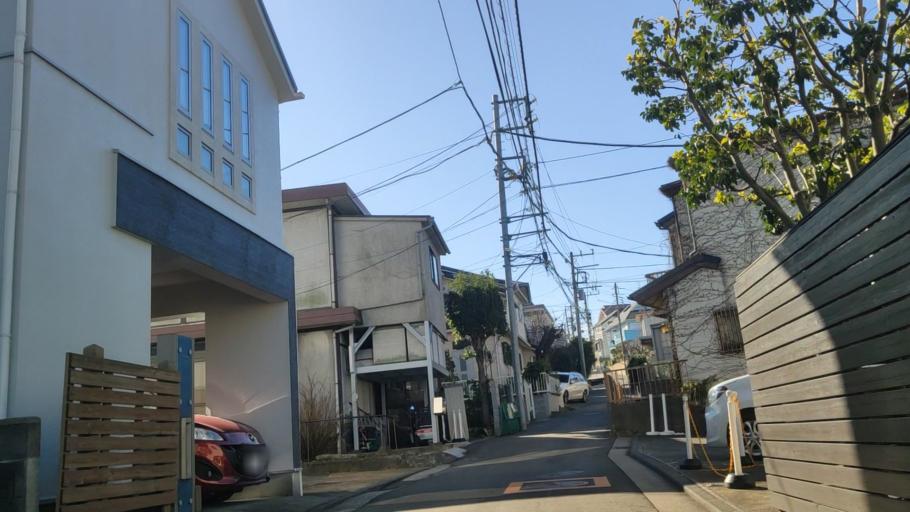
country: JP
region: Kanagawa
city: Yokohama
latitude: 35.4305
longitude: 139.6501
